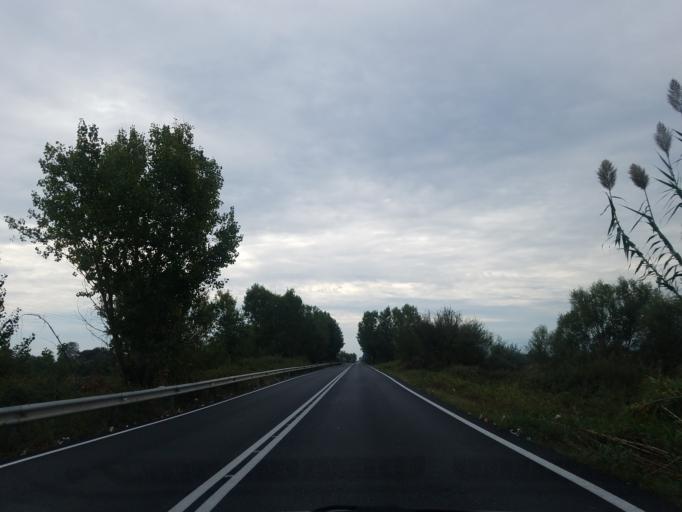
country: GR
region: Thessaly
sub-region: Nomos Kardhitsas
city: Agnantero
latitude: 39.4601
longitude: 21.8551
